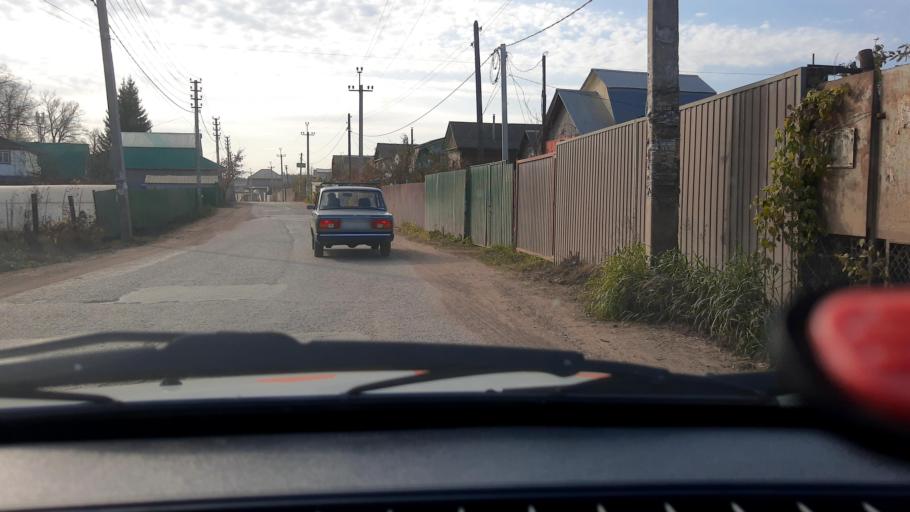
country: RU
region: Bashkortostan
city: Ufa
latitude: 54.6937
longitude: 55.9011
